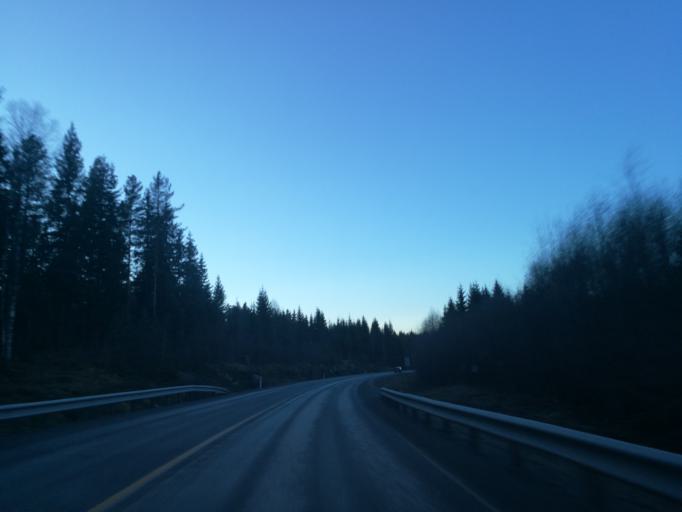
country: NO
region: Hedmark
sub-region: Eidskog
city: Skotterud
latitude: 59.9365
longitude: 12.1986
